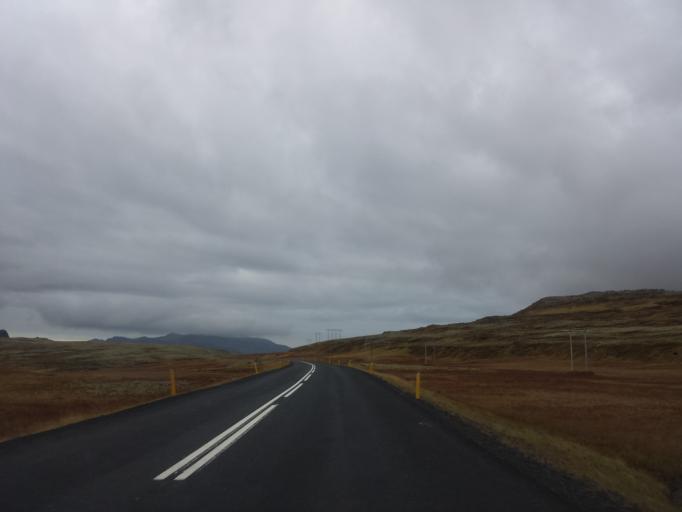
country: IS
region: West
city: Stykkisholmur
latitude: 64.9101
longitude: -22.8650
